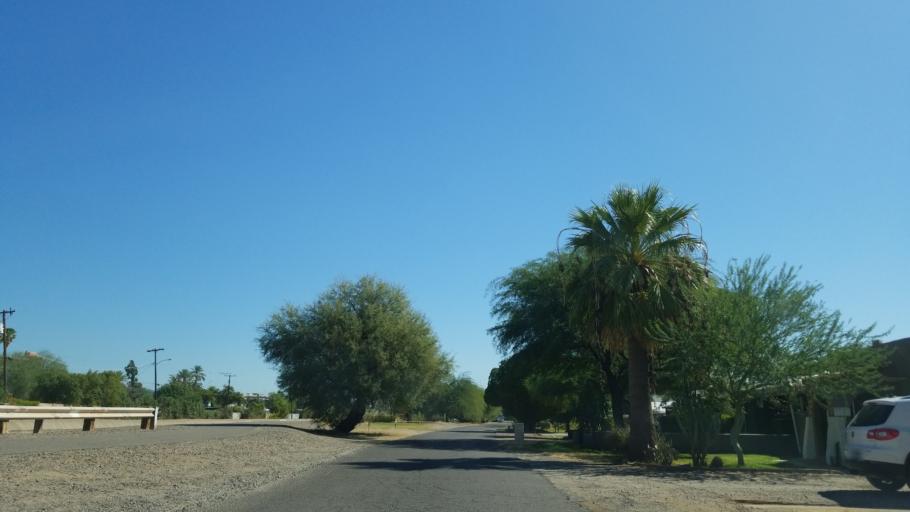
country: US
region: Arizona
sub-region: Maricopa County
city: Phoenix
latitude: 33.5029
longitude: -112.0808
